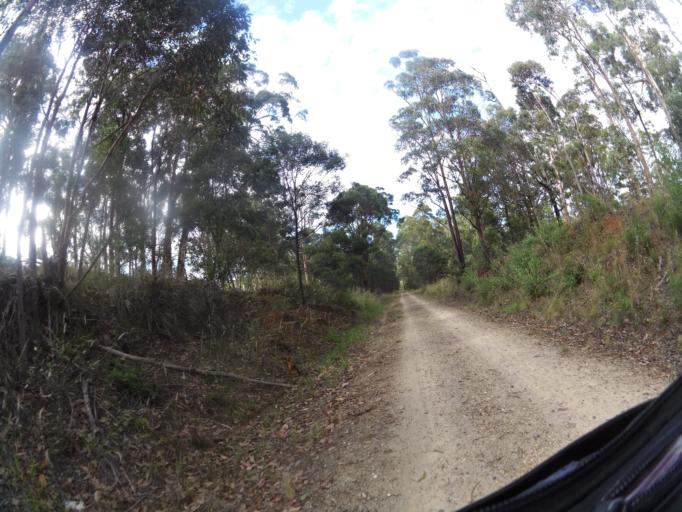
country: AU
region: Victoria
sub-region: East Gippsland
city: Lakes Entrance
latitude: -37.7374
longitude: 148.4212
